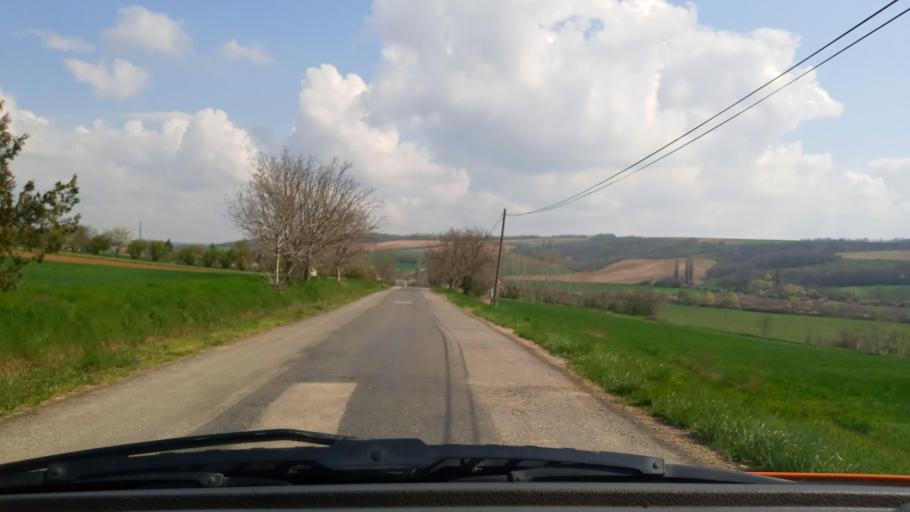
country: HU
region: Baranya
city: Pecsvarad
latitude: 46.0943
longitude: 18.4695
